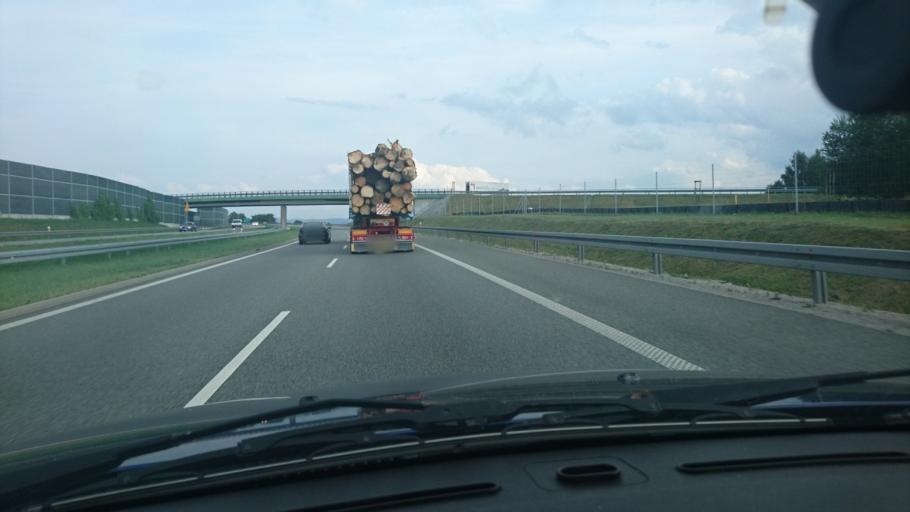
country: PL
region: Silesian Voivodeship
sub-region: Powiat bielski
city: Wilkowice
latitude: 49.7447
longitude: 19.0909
